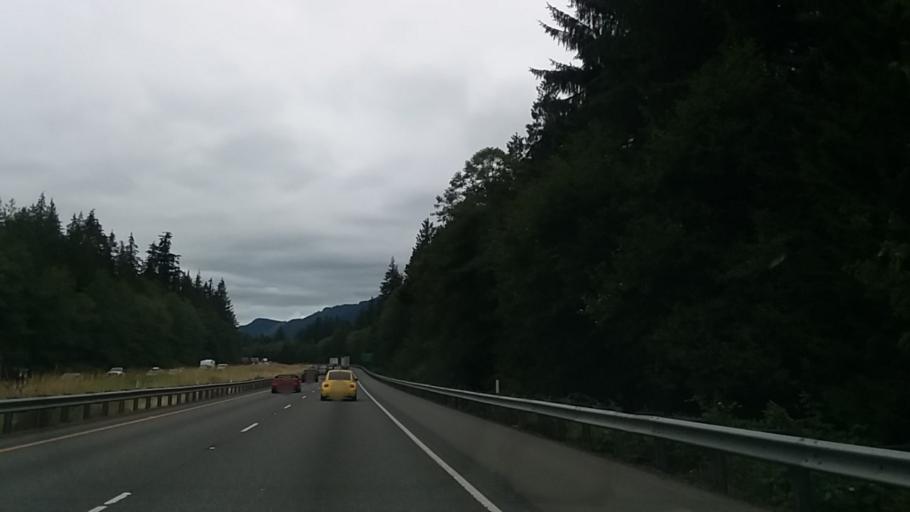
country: US
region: Washington
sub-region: Whatcom County
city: Sudden Valley
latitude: 48.6018
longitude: -122.3447
